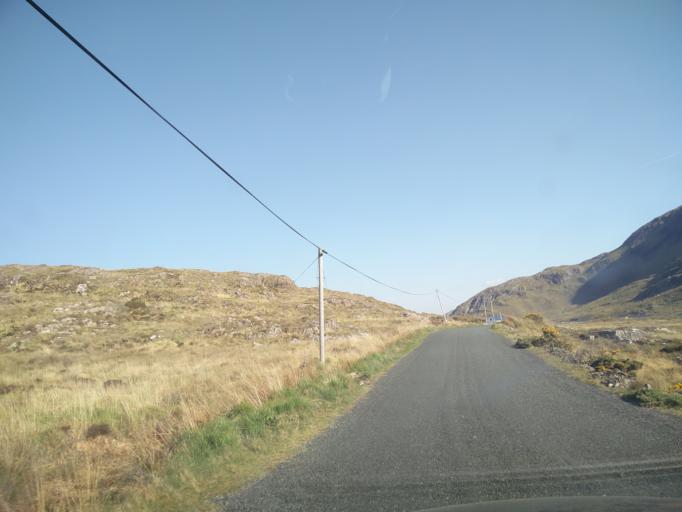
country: IE
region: Connaught
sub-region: County Galway
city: Clifden
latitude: 53.6046
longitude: -9.8602
